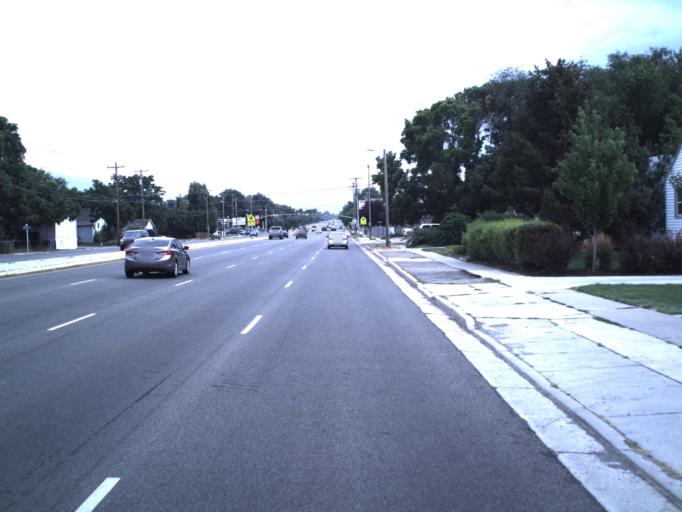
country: US
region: Utah
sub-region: Salt Lake County
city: Millcreek
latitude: 40.7030
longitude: -111.8715
